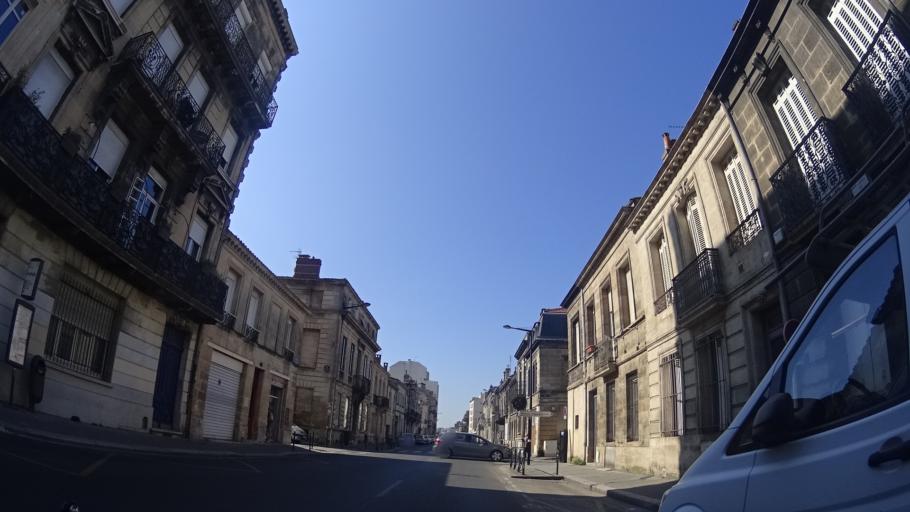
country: FR
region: Aquitaine
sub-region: Departement de la Gironde
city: Bordeaux
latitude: 44.8256
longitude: -0.5726
